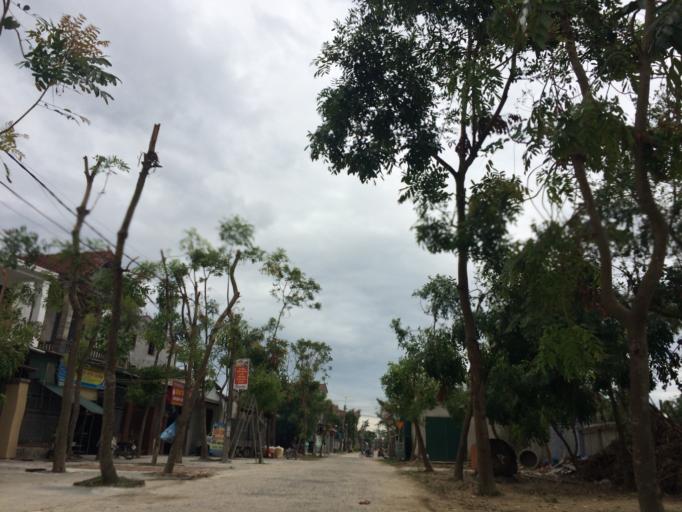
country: VN
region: Ha Tinh
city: Thach Ha
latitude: 18.3682
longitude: 105.8862
